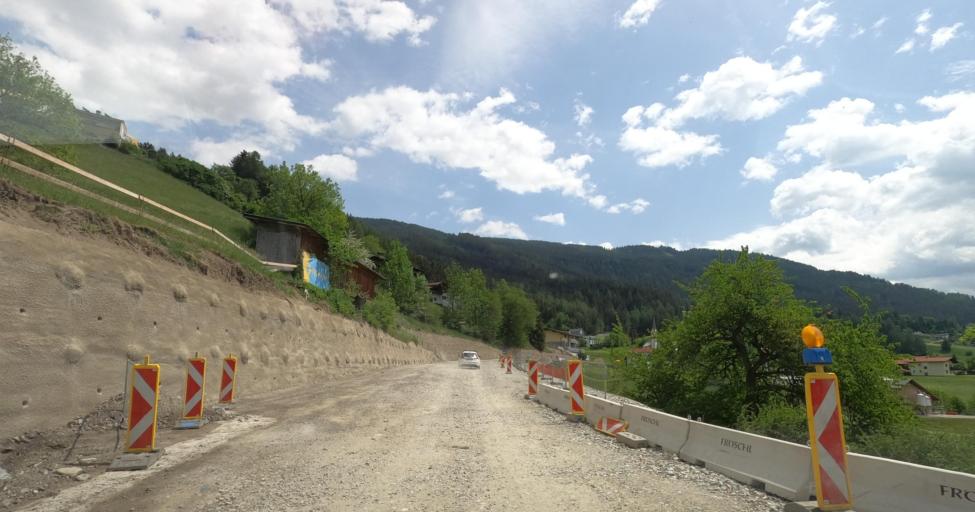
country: AT
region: Tyrol
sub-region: Politischer Bezirk Innsbruck Land
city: Pfons
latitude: 47.1447
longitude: 11.4578
